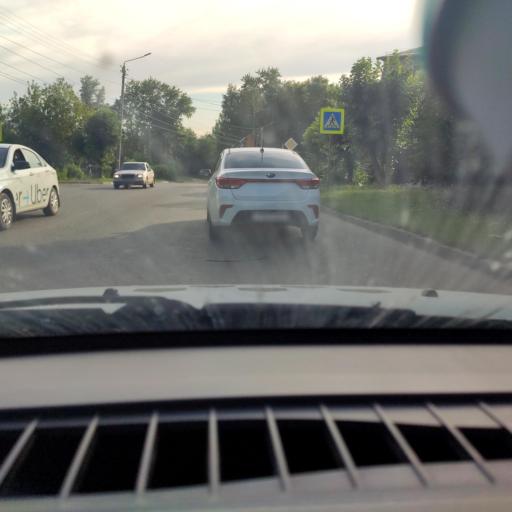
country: RU
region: Kirov
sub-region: Kirovo-Chepetskiy Rayon
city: Kirov
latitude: 58.6228
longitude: 49.6421
